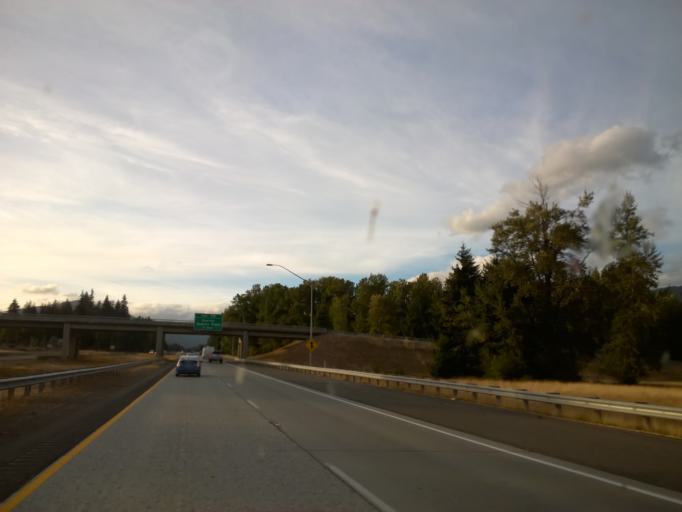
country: US
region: Washington
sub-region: Kittitas County
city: Cle Elum
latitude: 47.2361
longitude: -121.1731
